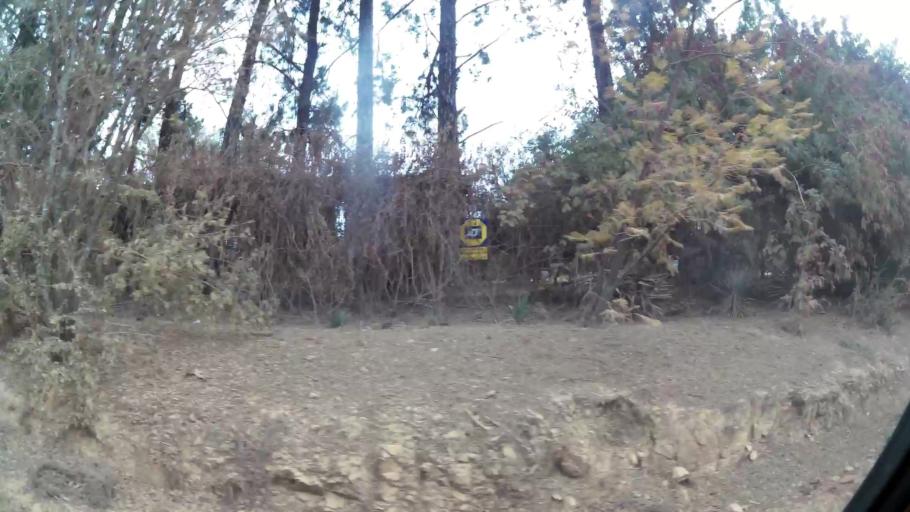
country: ZA
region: Gauteng
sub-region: West Rand District Municipality
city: Muldersdriseloop
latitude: -26.0743
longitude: 27.8784
